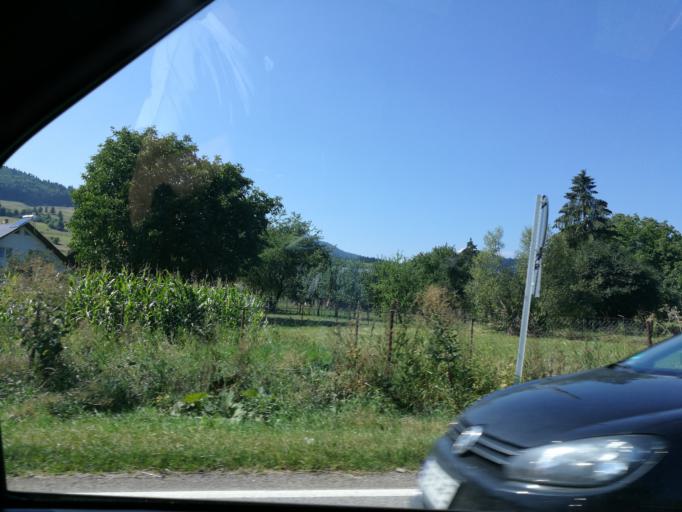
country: RO
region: Suceava
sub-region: Comuna Putna
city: Gura Putnei
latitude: 47.8932
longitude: 25.6103
